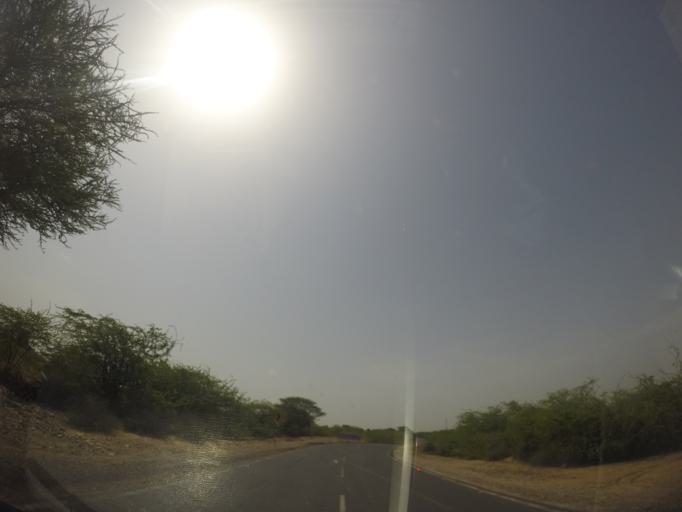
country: IN
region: Rajasthan
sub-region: Barmer
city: Barmer
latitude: 25.9627
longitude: 71.3697
